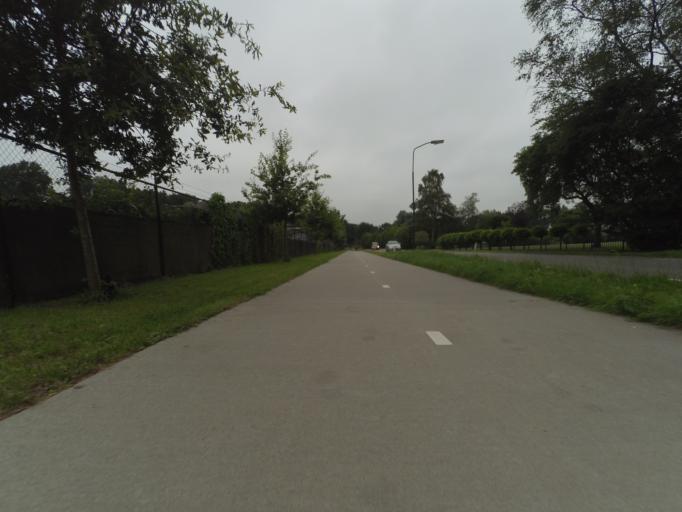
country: NL
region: Utrecht
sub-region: Gemeente Leusden
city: Leusden
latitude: 52.1344
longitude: 5.4483
